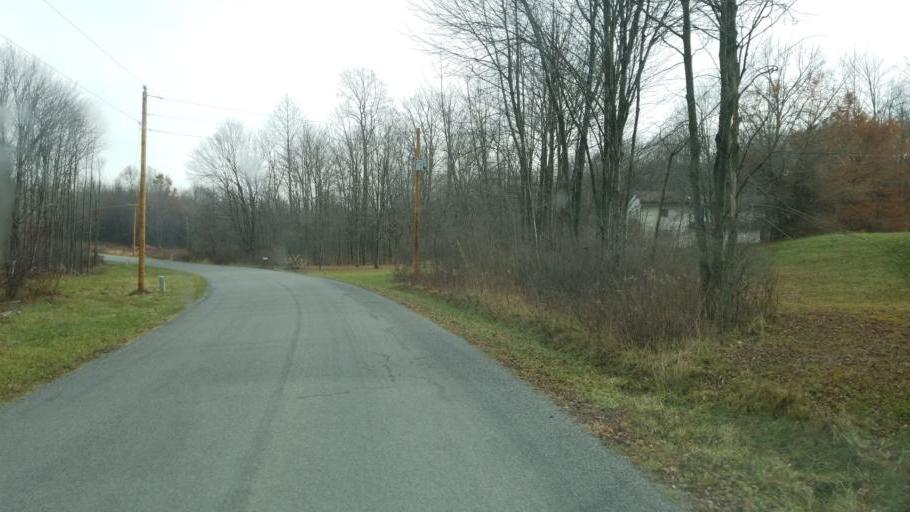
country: US
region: Pennsylvania
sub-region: Crawford County
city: Cochranton
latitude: 41.4898
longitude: -80.1233
